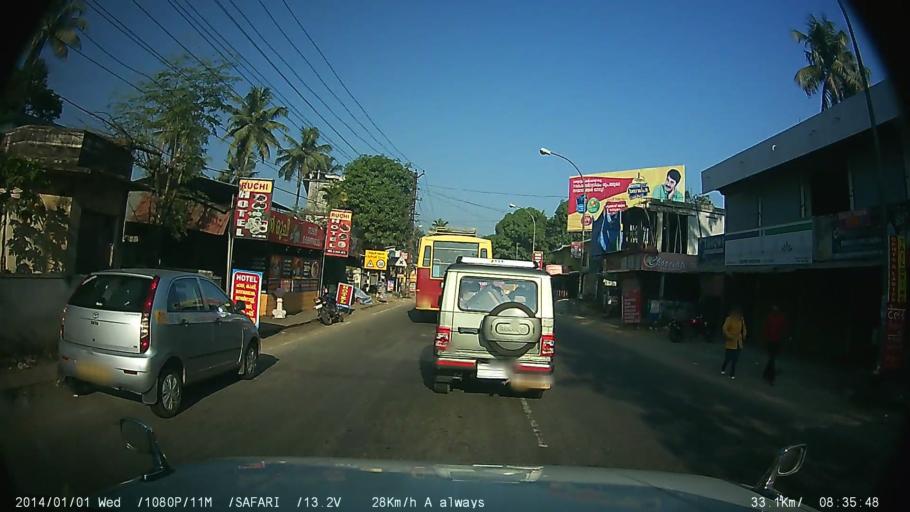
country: IN
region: Kerala
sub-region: Ernakulam
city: Perumpavur
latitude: 10.1365
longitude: 76.4668
